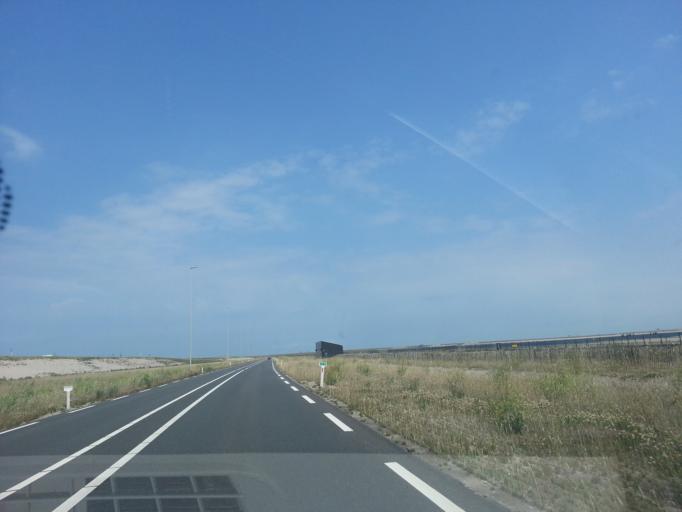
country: NL
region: South Holland
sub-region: Gemeente Goeree-Overflakkee
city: Goedereede
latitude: 51.9693
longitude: 3.9692
